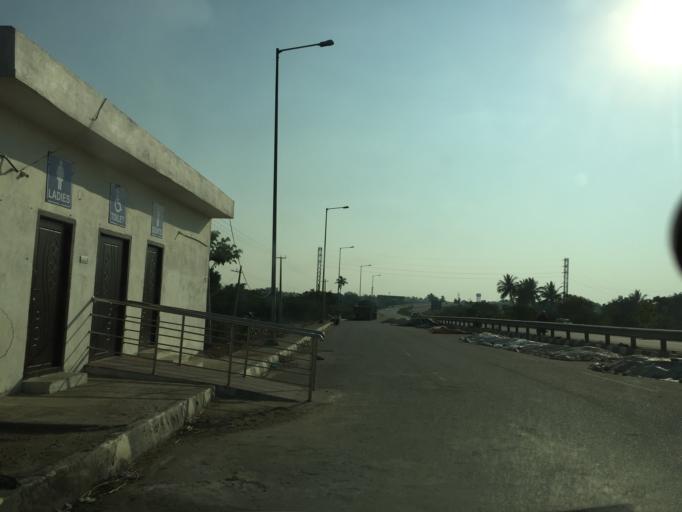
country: IN
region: Telangana
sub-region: Nalgonda
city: Bhongir
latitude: 17.5056
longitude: 78.8970
